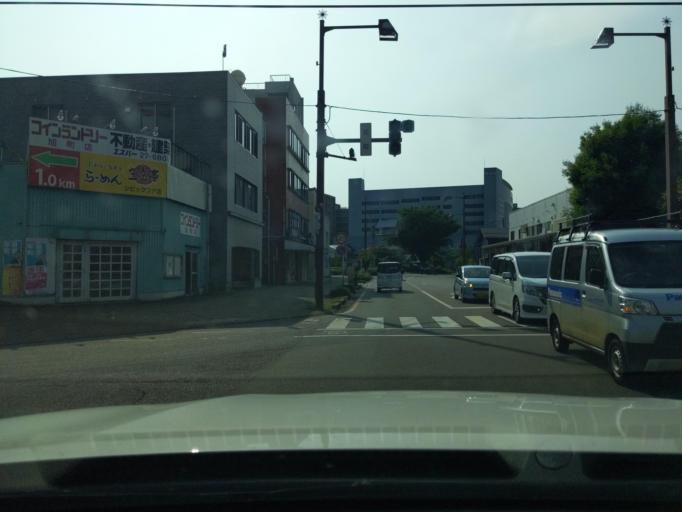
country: JP
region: Niigata
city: Nagaoka
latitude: 37.4431
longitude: 138.8510
